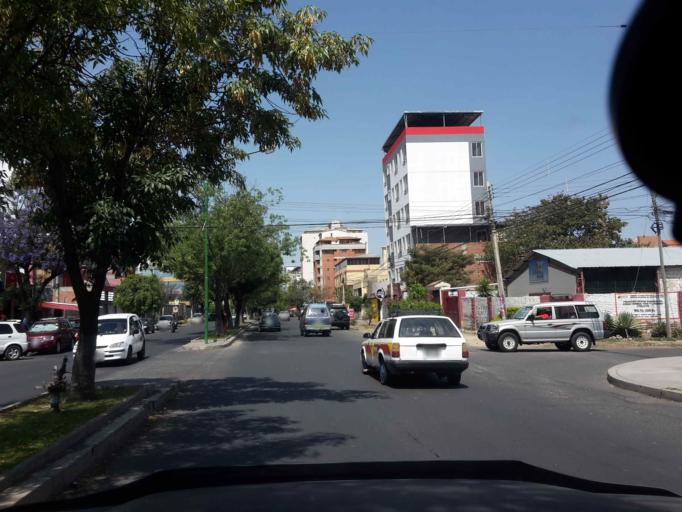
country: BO
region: Cochabamba
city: Cochabamba
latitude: -17.3718
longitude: -66.1784
